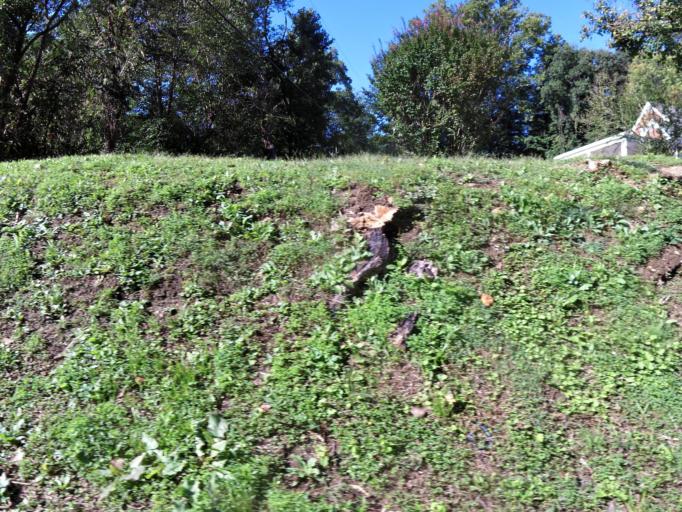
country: US
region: Kentucky
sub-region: Whitley County
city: Williamsburg
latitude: 36.7416
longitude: -84.1647
